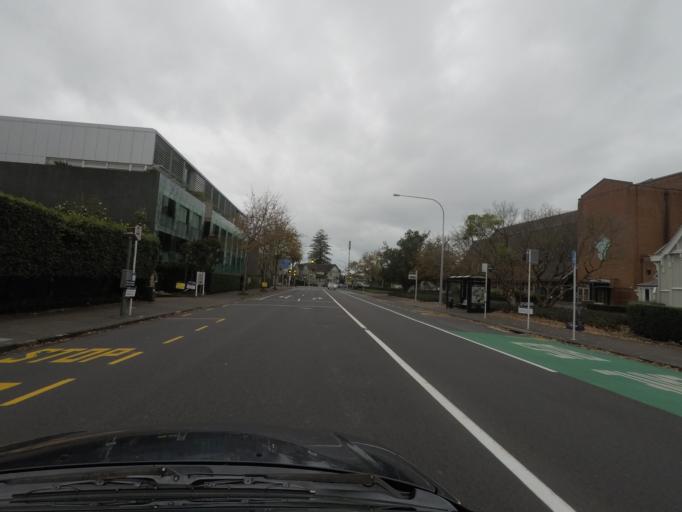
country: NZ
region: Auckland
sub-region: Auckland
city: Auckland
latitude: -36.8602
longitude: 174.7828
